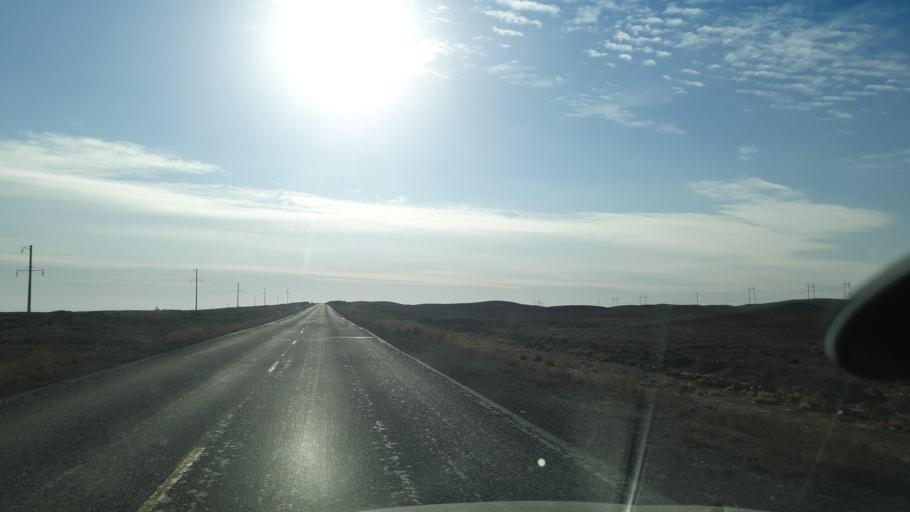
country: KZ
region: Zhambyl
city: Mynaral
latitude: 45.7143
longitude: 73.4013
